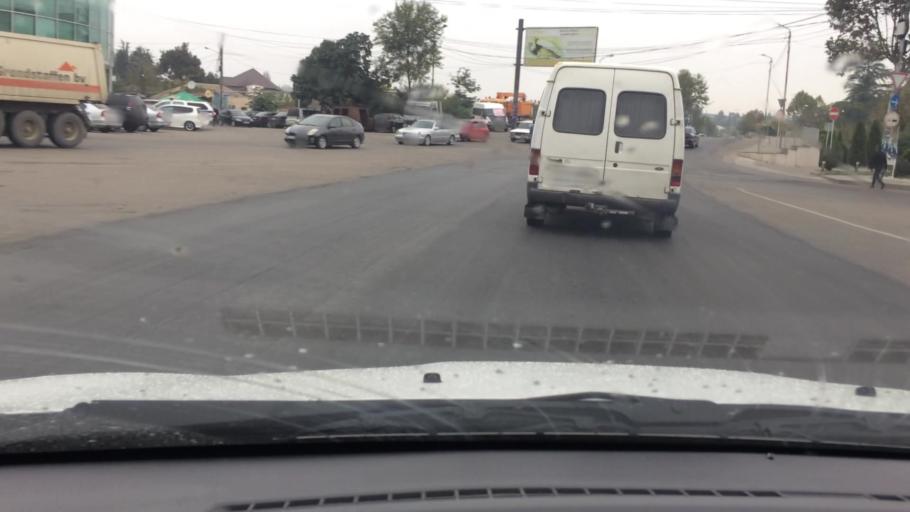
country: GE
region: Kvemo Kartli
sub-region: Marneuli
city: Marneuli
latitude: 41.4878
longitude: 44.7988
